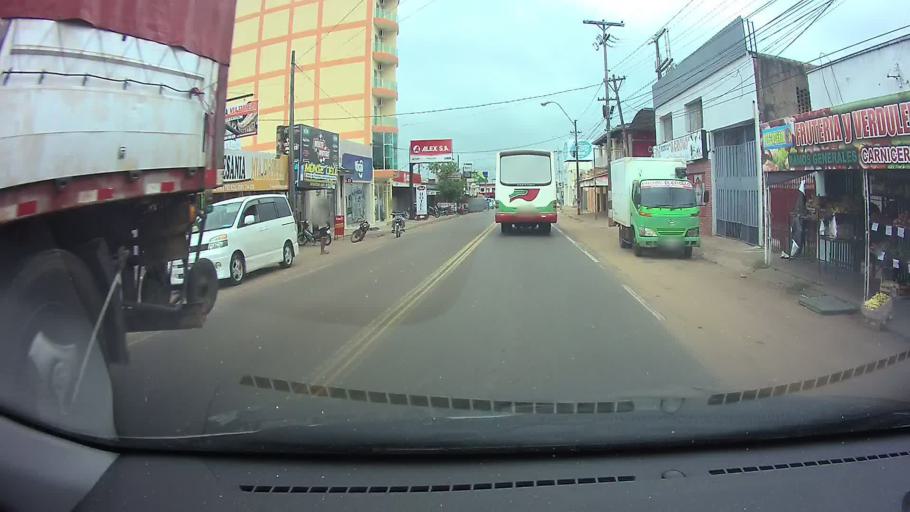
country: PY
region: Paraguari
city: Carapegua
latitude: -25.7673
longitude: -57.2386
